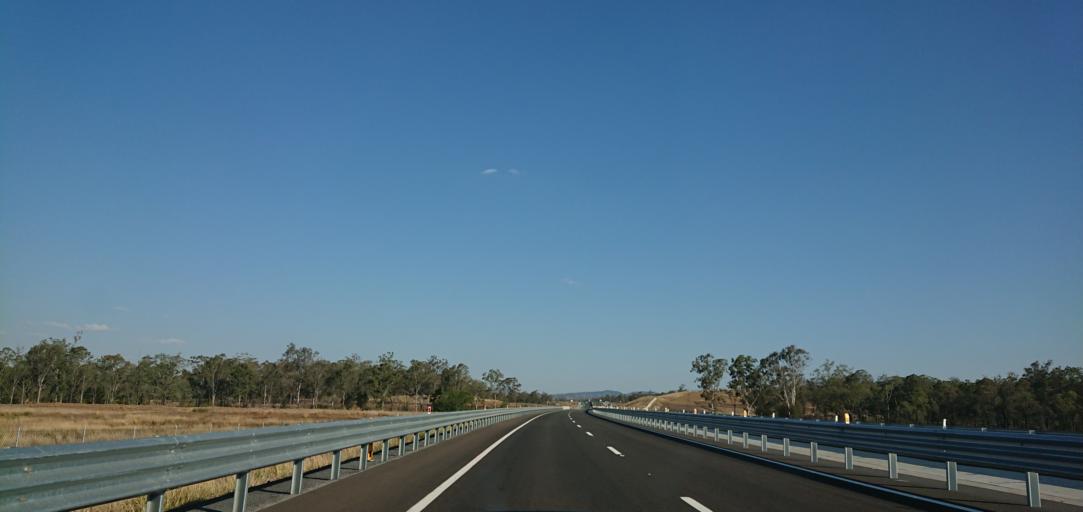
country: AU
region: Queensland
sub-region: Toowoomba
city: Rangeville
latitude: -27.5338
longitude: 152.0753
